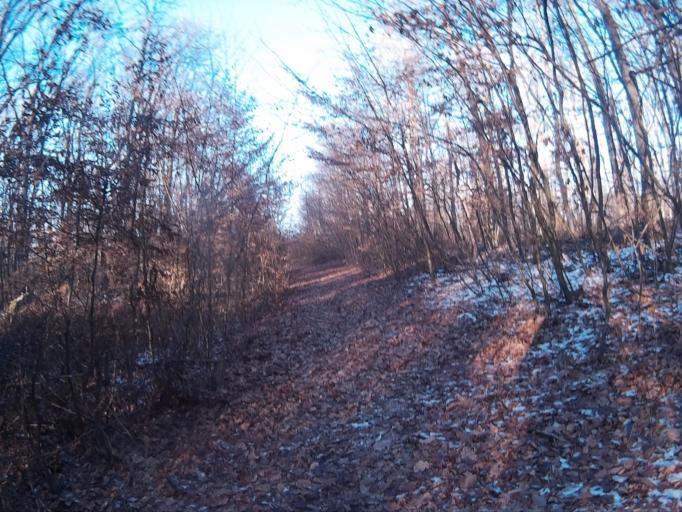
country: HU
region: Borsod-Abauj-Zemplen
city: Putnok
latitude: 48.4571
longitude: 20.4699
